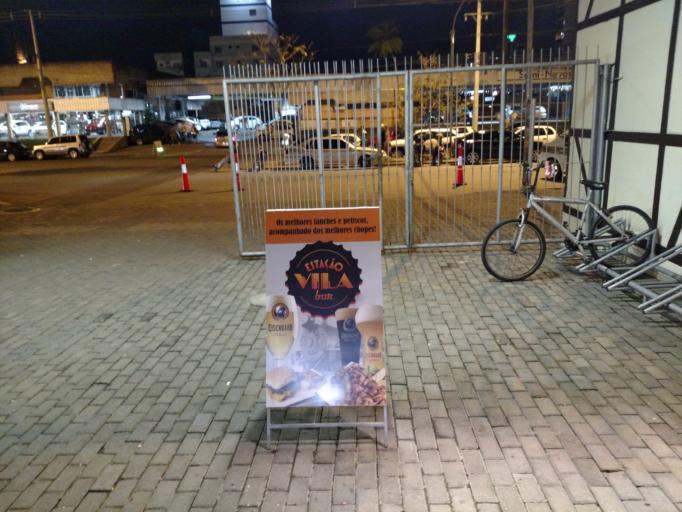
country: BR
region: Santa Catarina
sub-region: Blumenau
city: Blumenau
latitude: -26.9151
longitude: -49.0847
